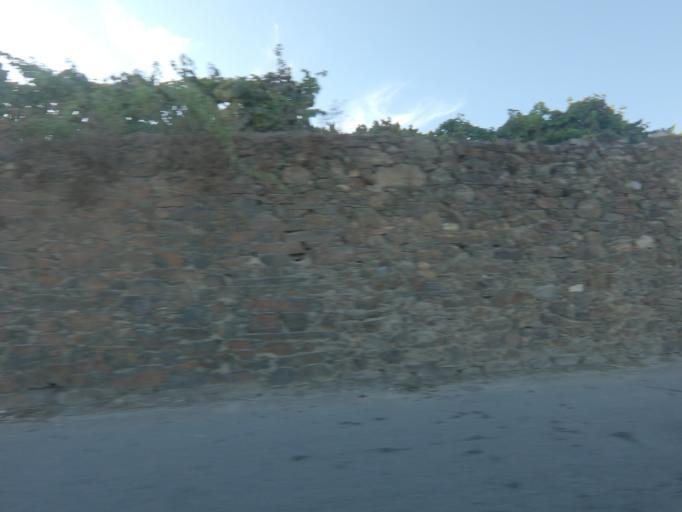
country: PT
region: Vila Real
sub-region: Peso da Regua
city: Godim
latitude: 41.1699
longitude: -7.8067
